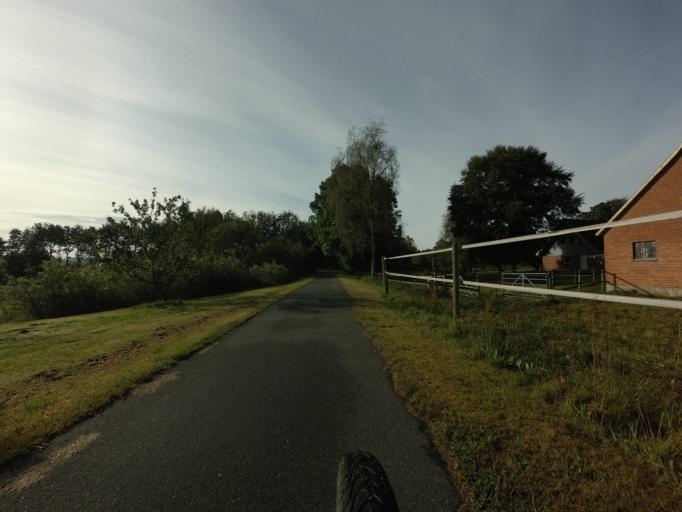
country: DK
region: Central Jutland
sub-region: Viborg Kommune
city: Viborg
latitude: 56.4272
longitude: 9.4548
